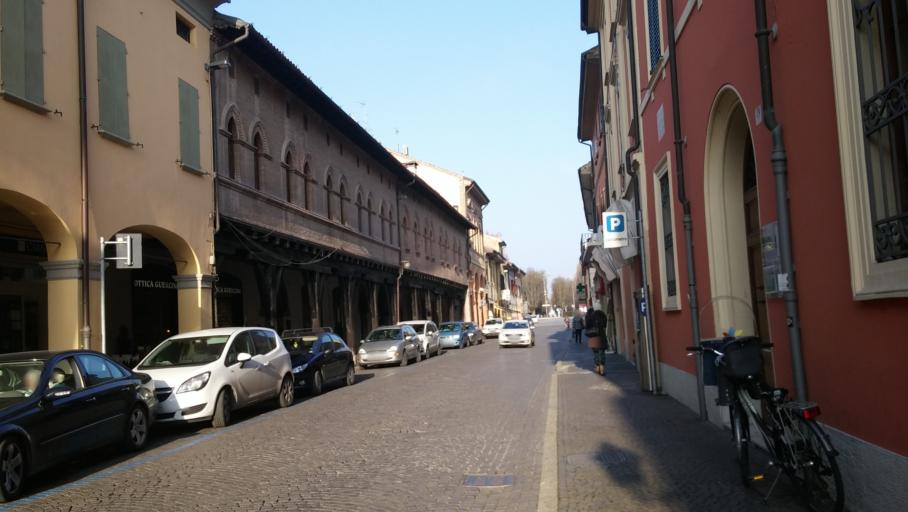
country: IT
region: Emilia-Romagna
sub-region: Provincia di Ferrara
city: Cento
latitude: 44.7284
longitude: 11.2917
